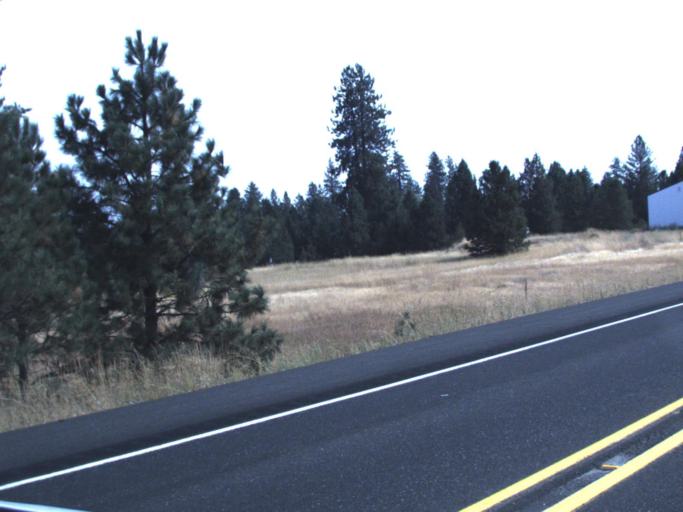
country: US
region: Washington
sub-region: Spokane County
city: Deer Park
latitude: 47.9105
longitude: -117.4464
